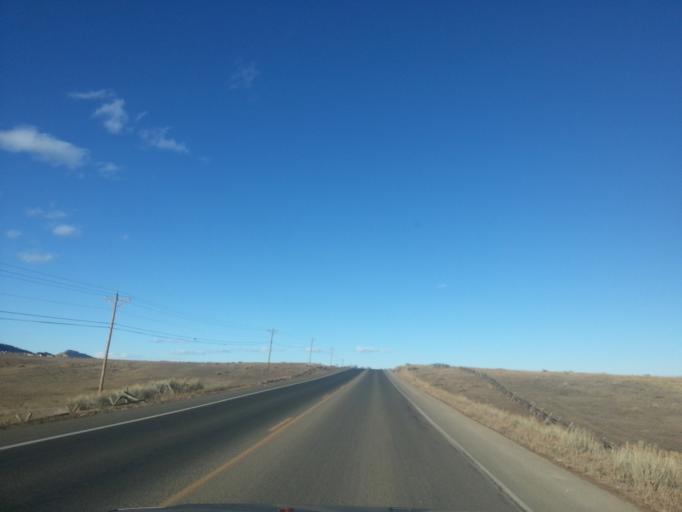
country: US
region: Colorado
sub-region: Larimer County
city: Fort Collins
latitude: 40.5100
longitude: -105.1153
